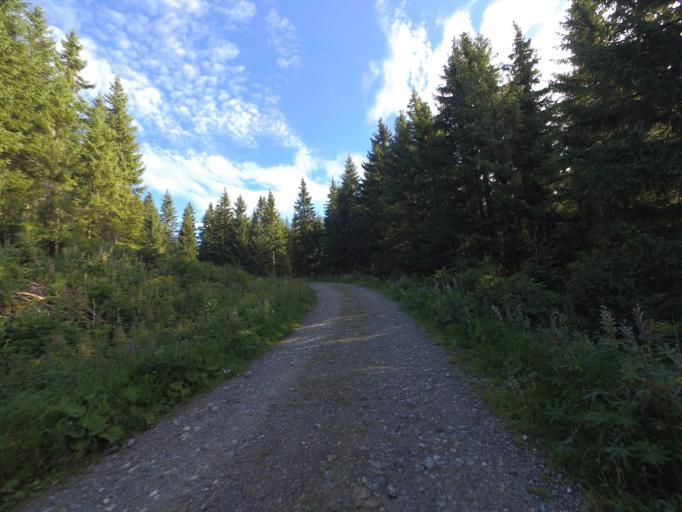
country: AT
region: Salzburg
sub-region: Politischer Bezirk Sankt Johann im Pongau
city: Goldegg
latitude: 47.3480
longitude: 13.0951
